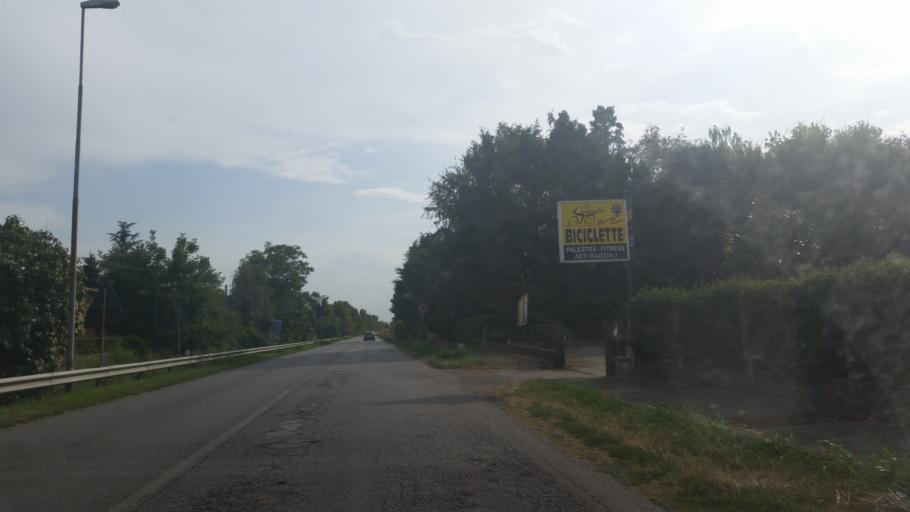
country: IT
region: Lombardy
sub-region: Provincia di Brescia
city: Dello
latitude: 45.4165
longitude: 10.0799
